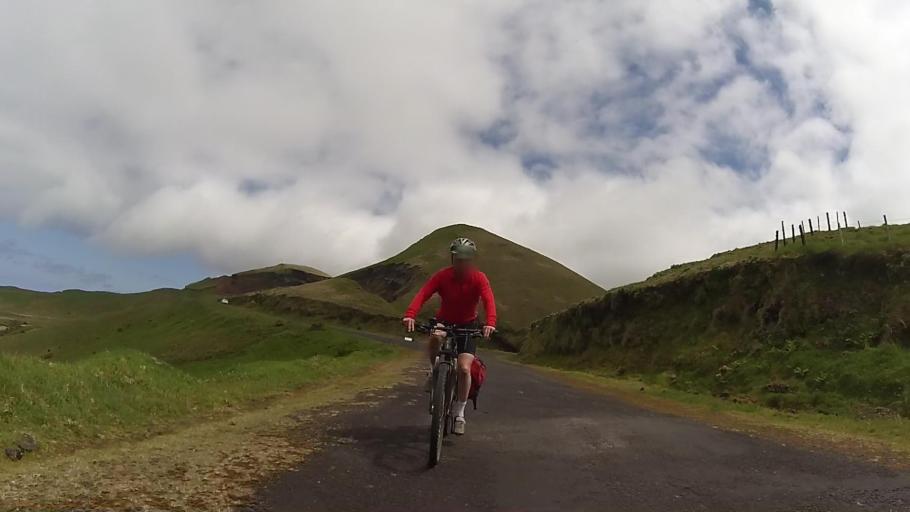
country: PT
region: Azores
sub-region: Sao Roque do Pico
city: Sao Roque do Pico
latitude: 38.4481
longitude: -28.2345
